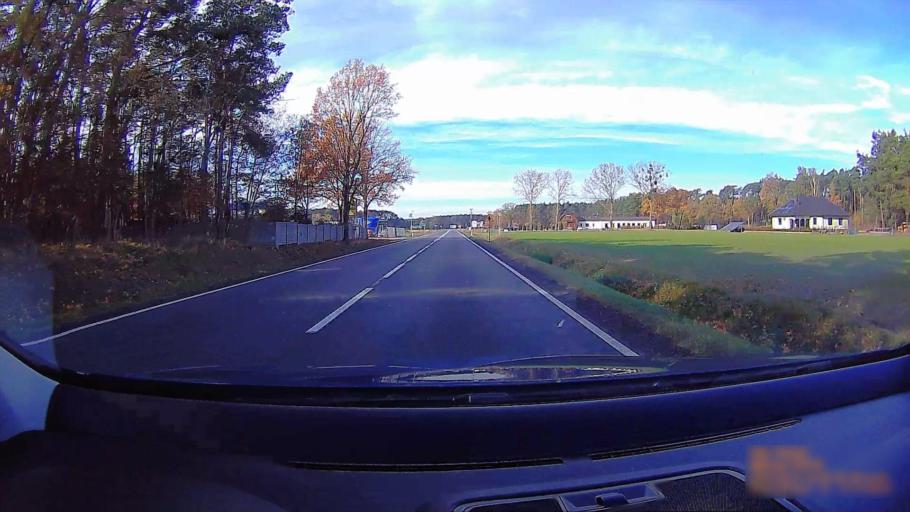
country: PL
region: Greater Poland Voivodeship
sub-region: Powiat ostrzeszowski
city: Ostrzeszow
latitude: 51.4880
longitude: 17.8636
